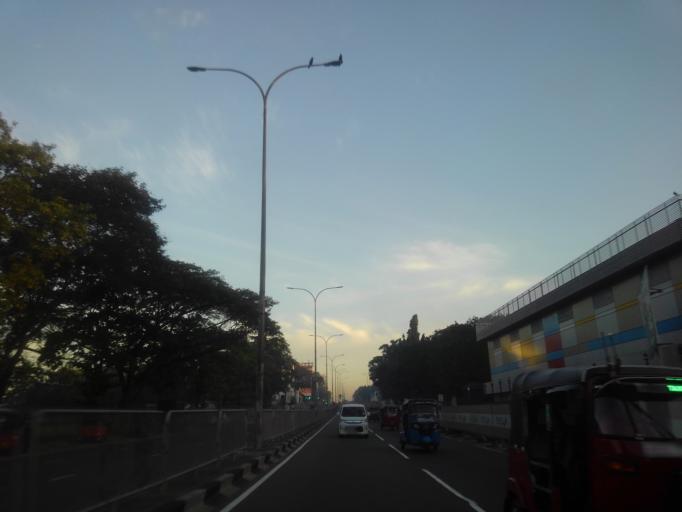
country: LK
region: Western
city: Kolonnawa
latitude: 6.9191
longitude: 79.8777
